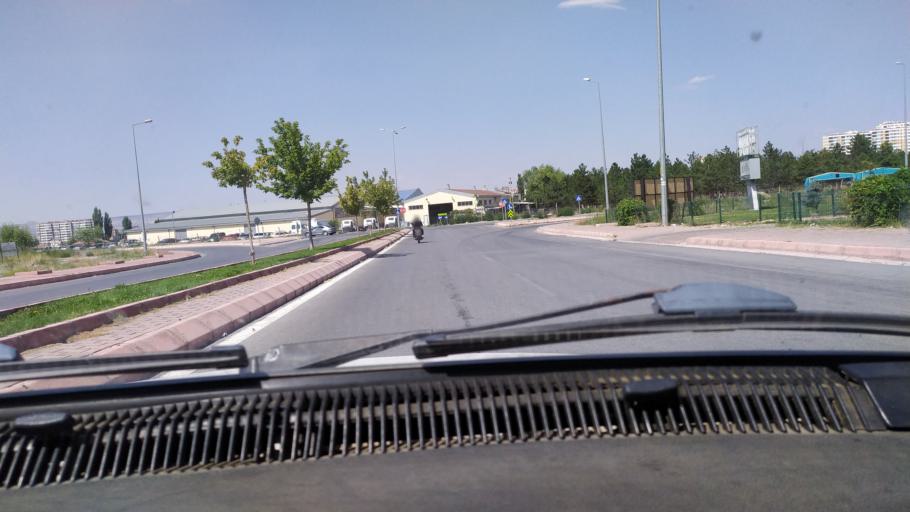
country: TR
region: Kayseri
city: Talas
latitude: 38.7189
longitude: 35.5552
